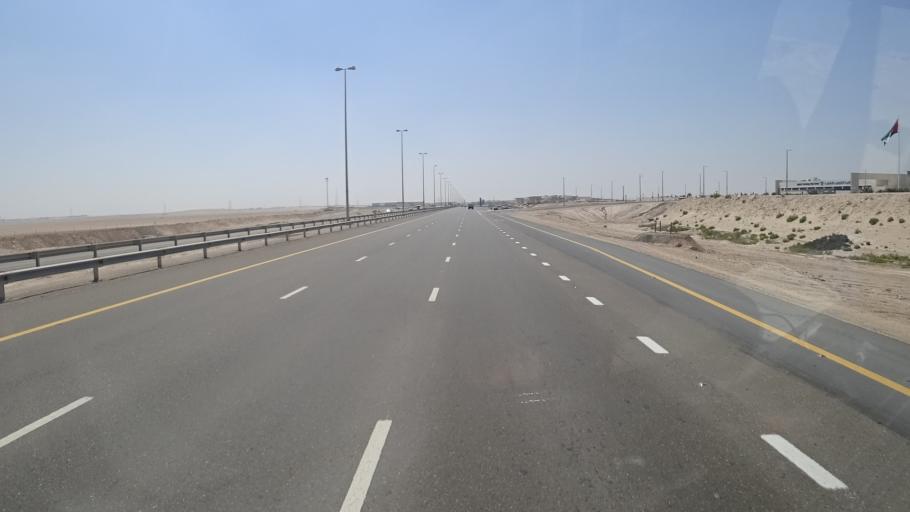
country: AE
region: Abu Dhabi
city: Abu Dhabi
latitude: 24.3221
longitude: 54.6852
